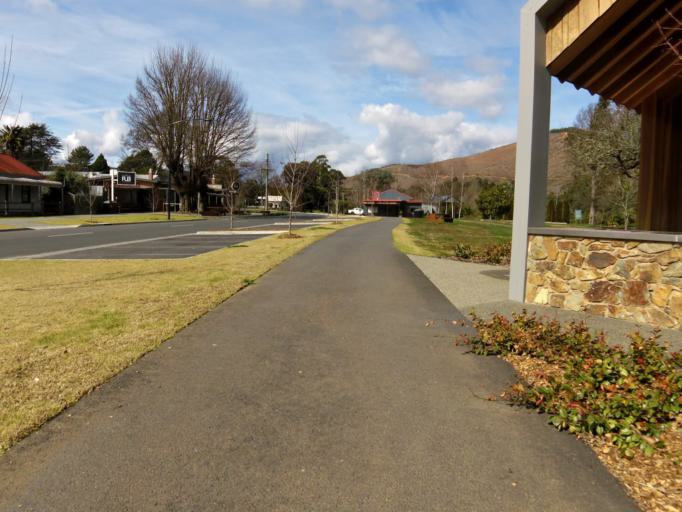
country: AU
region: Victoria
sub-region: Alpine
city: Mount Beauty
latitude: -36.7005
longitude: 146.9115
